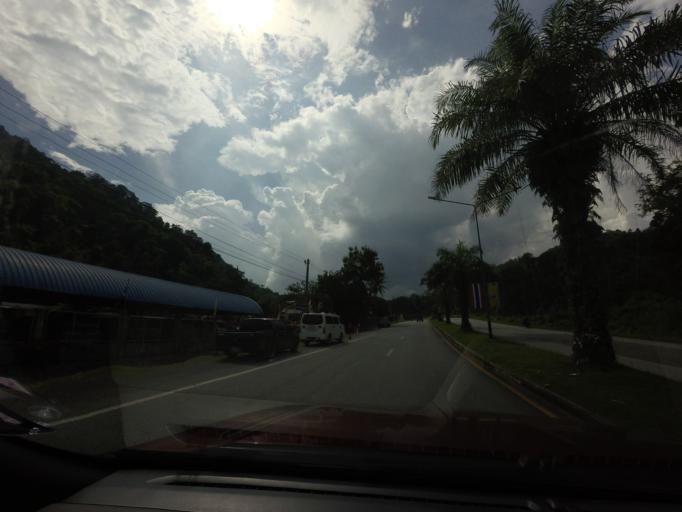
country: TH
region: Yala
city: Than To
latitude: 6.1712
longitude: 101.1788
